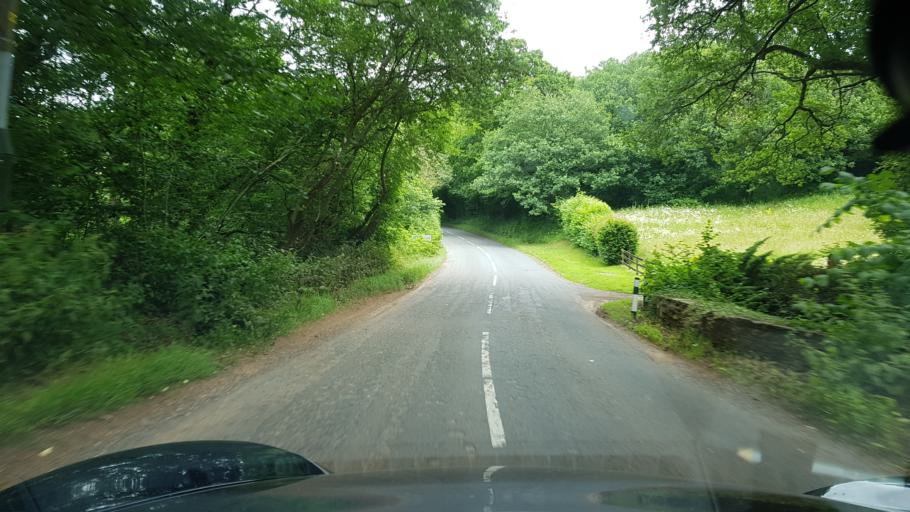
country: GB
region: England
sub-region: Herefordshire
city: Llanrothal
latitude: 51.8755
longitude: -2.8177
